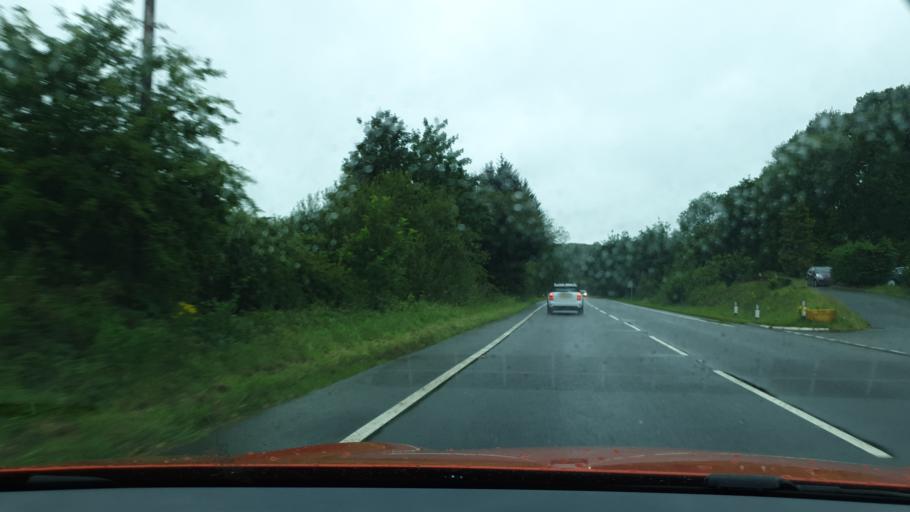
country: GB
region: England
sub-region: Cumbria
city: Ulverston
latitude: 54.2495
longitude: -3.0329
